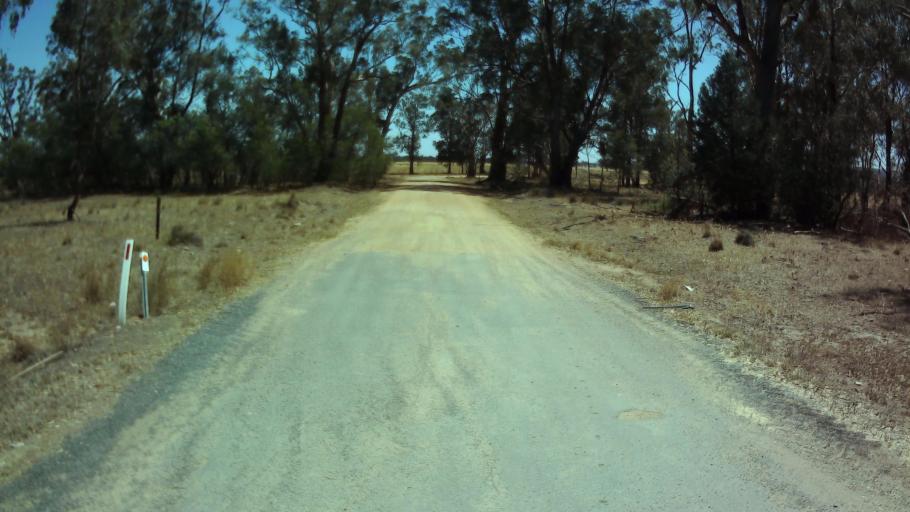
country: AU
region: New South Wales
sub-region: Weddin
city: Grenfell
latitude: -34.0280
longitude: 147.9620
